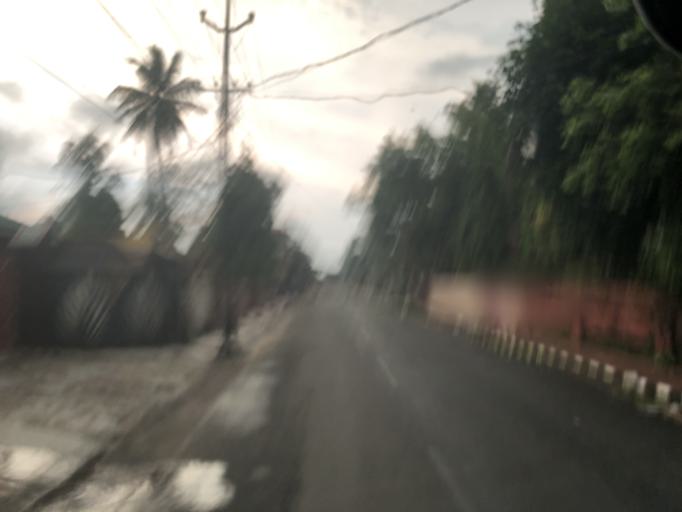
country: IN
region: Kerala
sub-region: Ernakulam
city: Cochin
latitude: 9.9520
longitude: 76.2546
